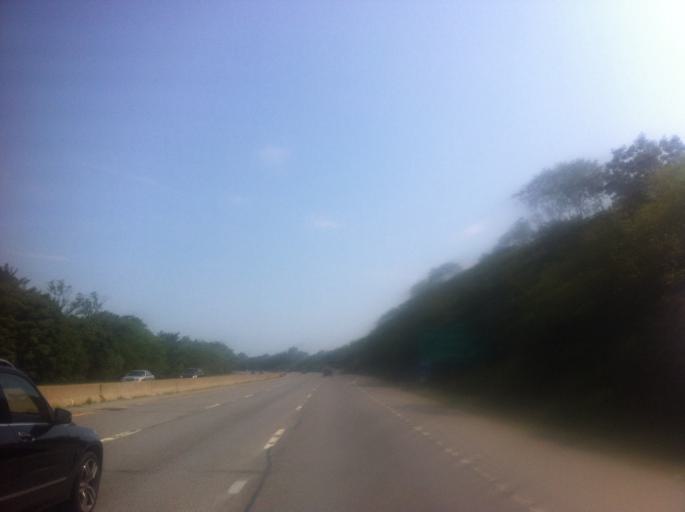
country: US
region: New York
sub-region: Nassau County
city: Plainview
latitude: 40.7865
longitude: -73.4845
